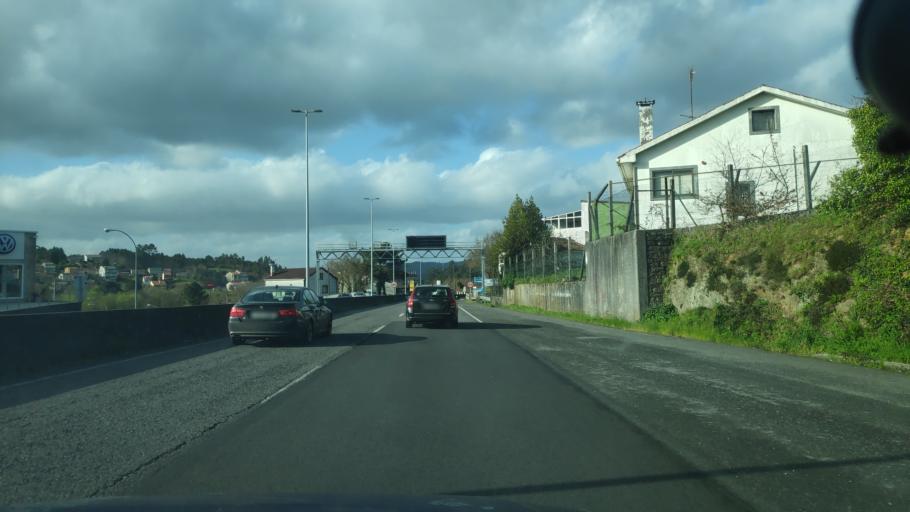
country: ES
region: Galicia
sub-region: Provincia da Coruna
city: Santiago de Compostela
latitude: 42.8571
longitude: -8.5712
